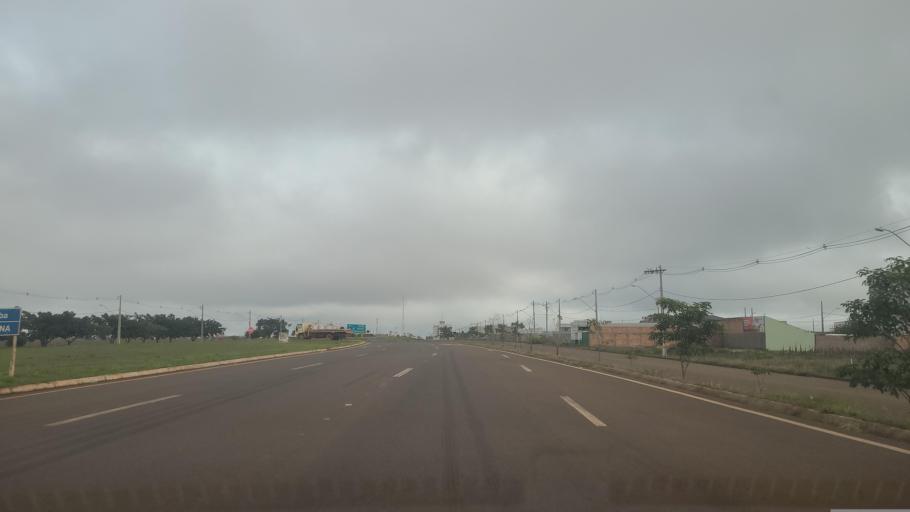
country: BR
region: Minas Gerais
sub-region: Sao Gotardo
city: Sao Gotardo
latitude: -19.2082
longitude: -46.2285
